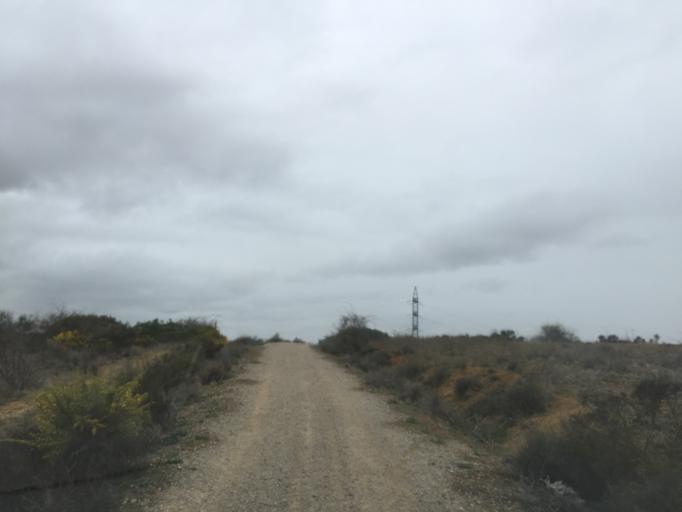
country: ES
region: Castille and Leon
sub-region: Provincia de Leon
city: Leon
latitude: 42.5962
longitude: -5.5392
